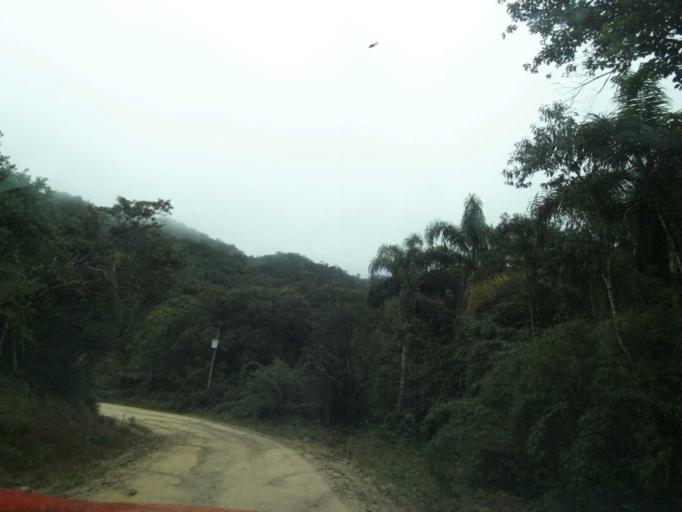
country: BR
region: Santa Catarina
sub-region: Anitapolis
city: Anitapolis
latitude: -27.9192
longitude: -49.1922
